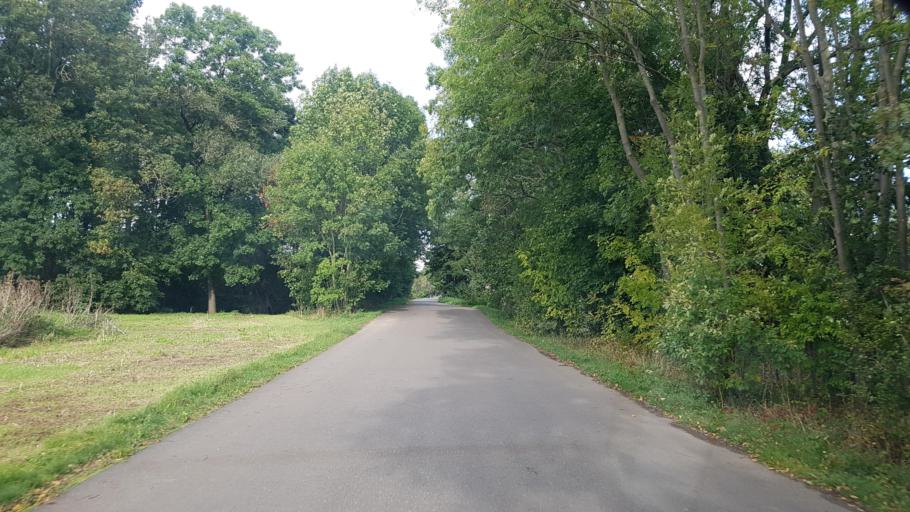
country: DE
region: Saxony
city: Groitzsch
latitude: 51.1608
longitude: 12.2685
